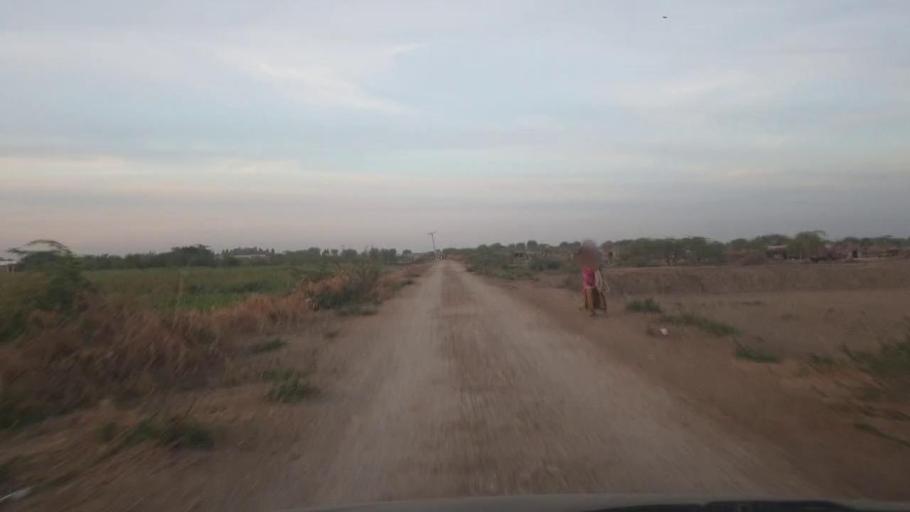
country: PK
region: Sindh
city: Kunri
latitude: 25.2346
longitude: 69.5202
